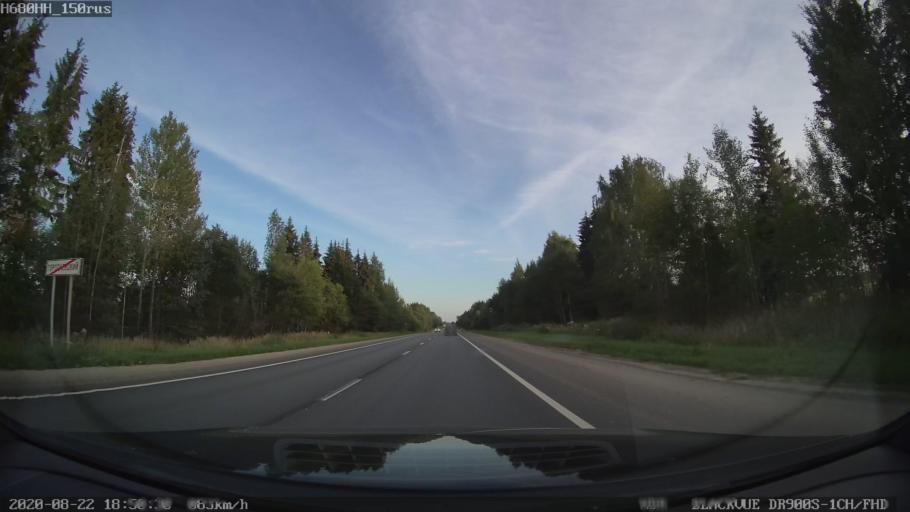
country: RU
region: Tverskaya
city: Rameshki
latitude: 57.2659
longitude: 36.0751
